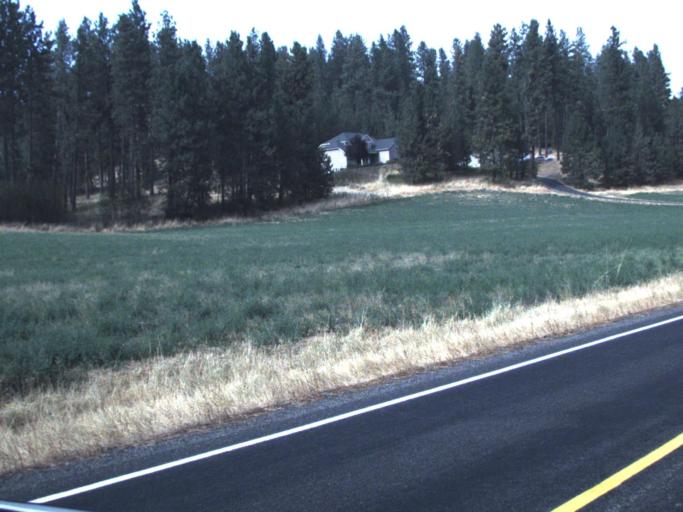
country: US
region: Washington
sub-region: Spokane County
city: Trentwood
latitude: 47.7992
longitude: -117.2394
